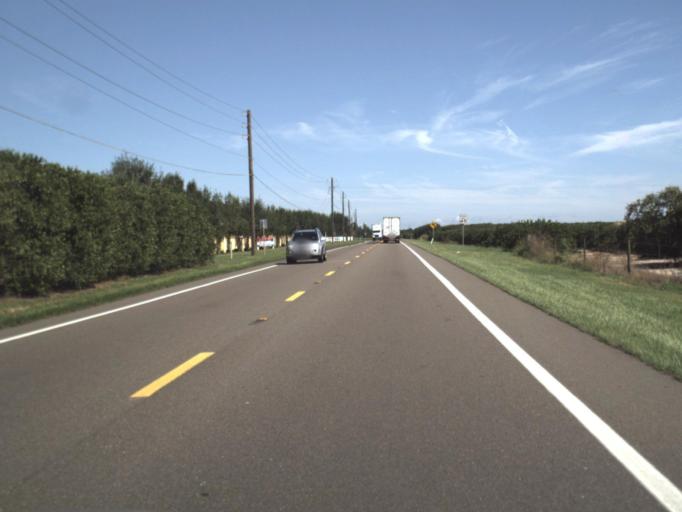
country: US
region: Florida
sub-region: Polk County
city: Auburndale
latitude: 28.1223
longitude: -81.7893
